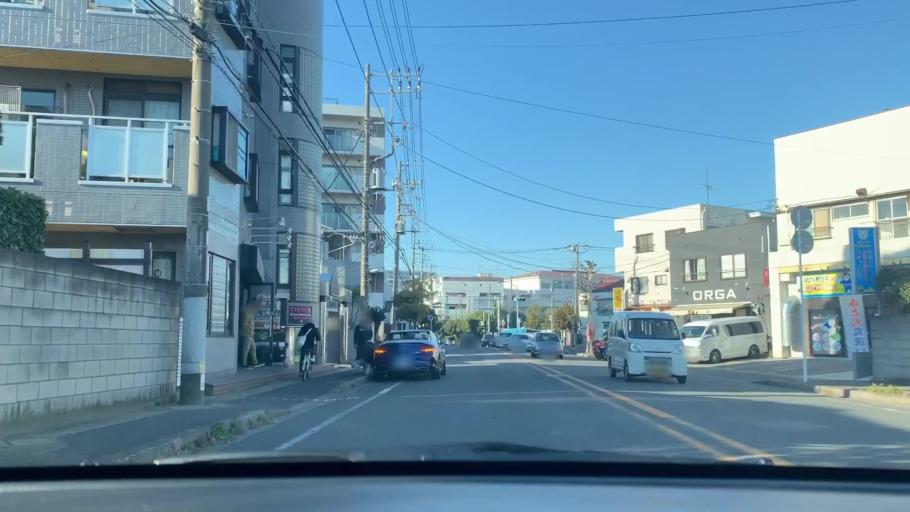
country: JP
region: Tokyo
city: Urayasu
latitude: 35.7193
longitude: 139.9089
